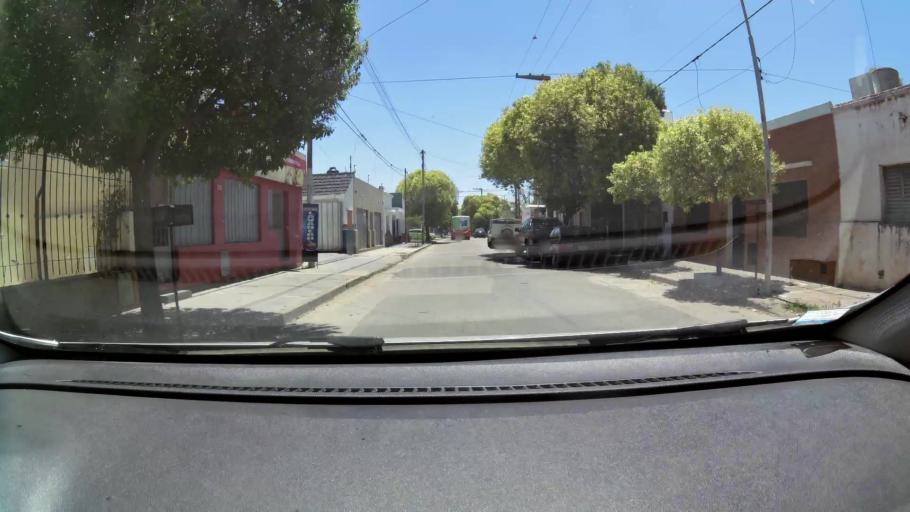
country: AR
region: Cordoba
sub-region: Departamento de Capital
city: Cordoba
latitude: -31.3829
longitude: -64.1333
